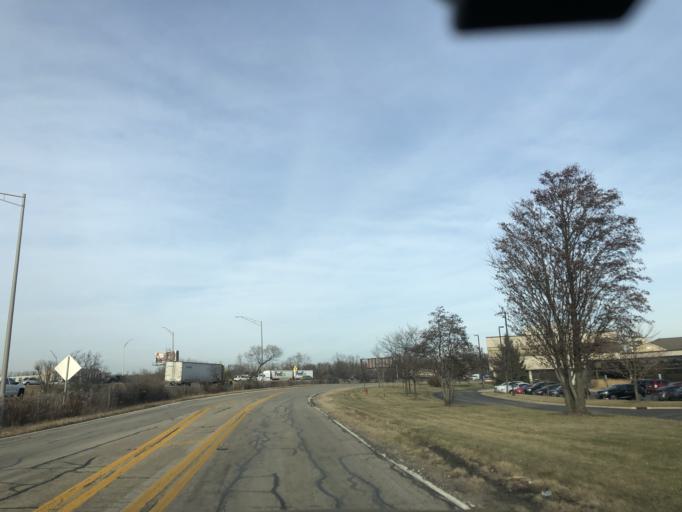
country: US
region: Illinois
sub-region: Cook County
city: Lemont
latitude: 41.7167
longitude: -88.0038
